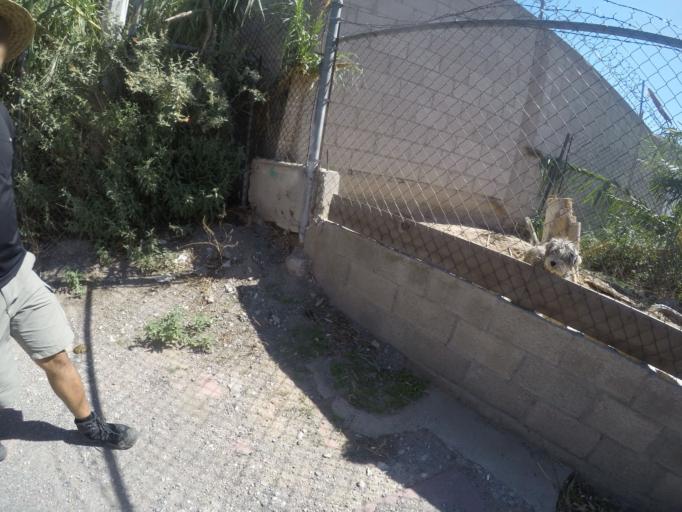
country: MX
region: Chihuahua
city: Ciudad Juarez
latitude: 31.7397
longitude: -106.4691
